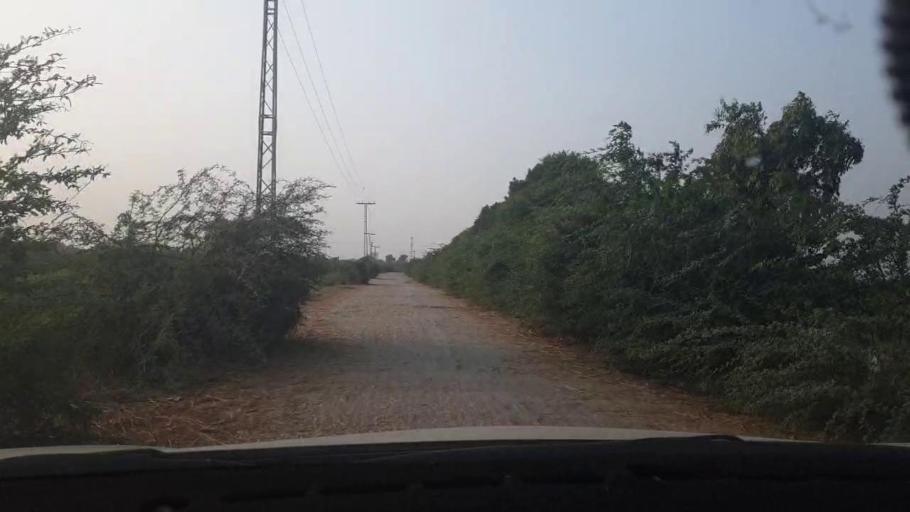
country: PK
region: Sindh
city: Bulri
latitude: 24.8561
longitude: 68.3370
